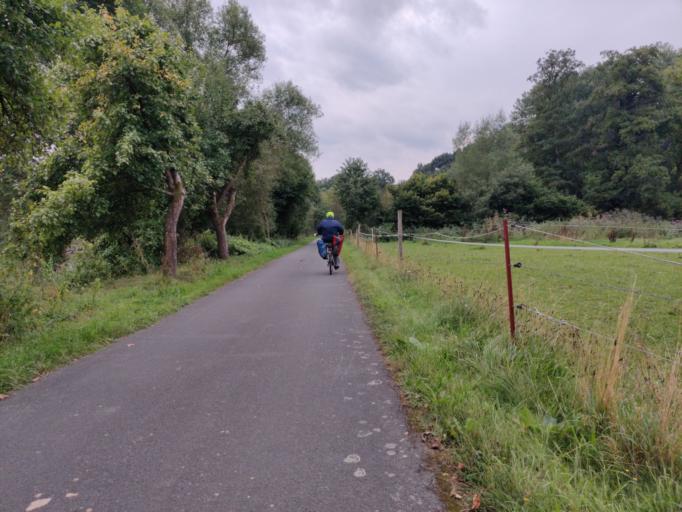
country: DE
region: North Rhine-Westphalia
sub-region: Regierungsbezirk Detmold
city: Hoexter
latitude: 51.8113
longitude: 9.4042
